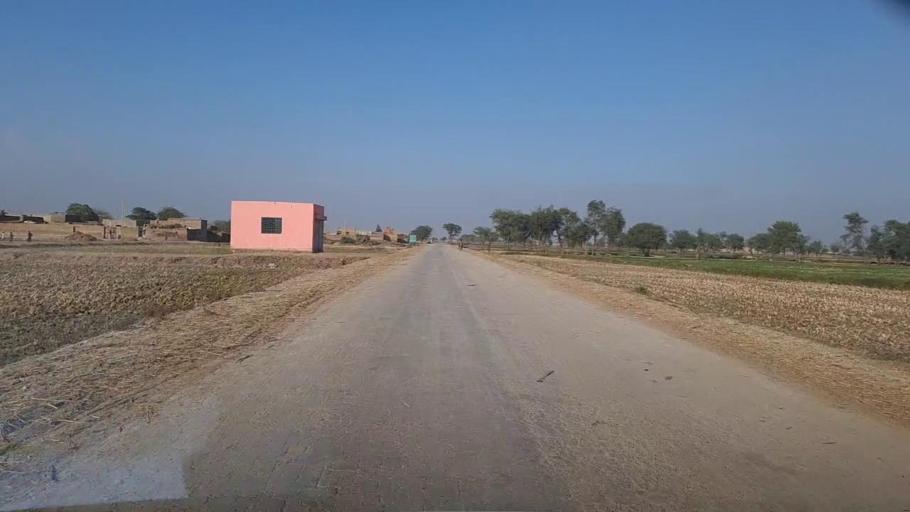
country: PK
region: Sindh
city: Phulji
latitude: 26.8589
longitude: 67.7942
